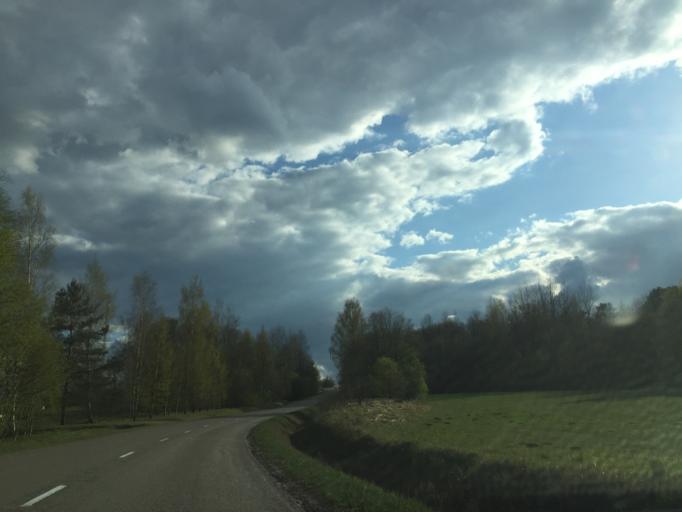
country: LV
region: Priekuli
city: Priekuli
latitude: 57.3851
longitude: 25.4385
